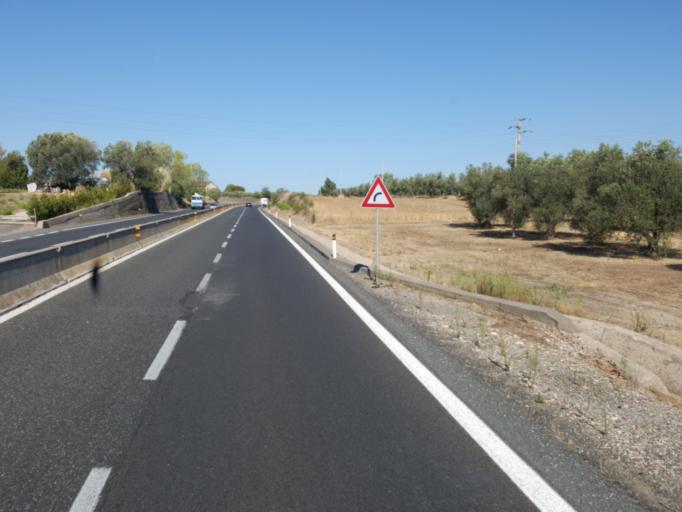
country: IT
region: Latium
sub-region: Provincia di Viterbo
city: Pescia Romana
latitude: 42.4068
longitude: 11.4841
